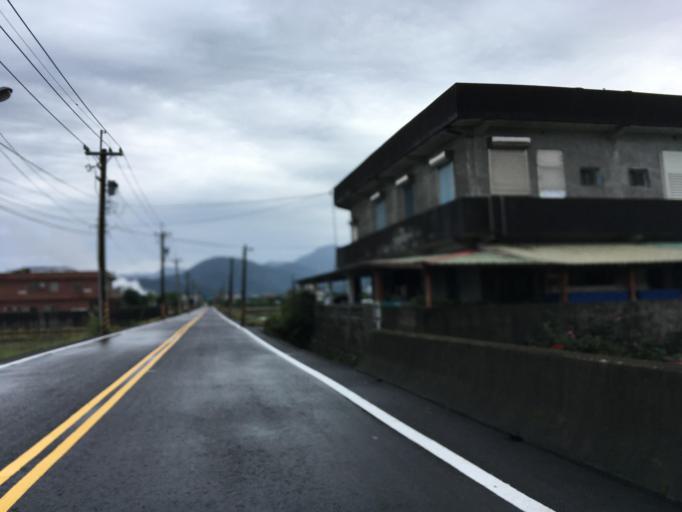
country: TW
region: Taiwan
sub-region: Yilan
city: Yilan
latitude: 24.6413
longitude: 121.8077
